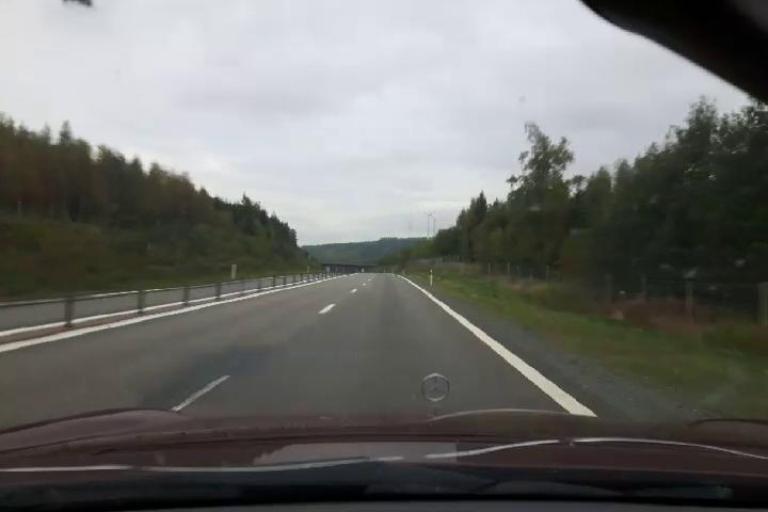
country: SE
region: Vaesternorrland
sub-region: Haernoesands Kommun
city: Haernoesand
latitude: 62.7608
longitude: 17.9049
